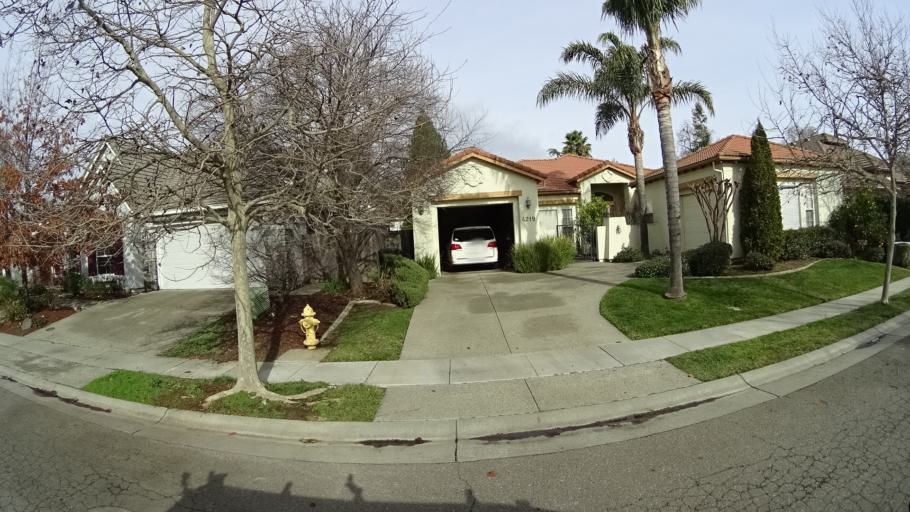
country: US
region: California
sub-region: Yolo County
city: Davis
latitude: 38.5455
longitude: -121.6996
